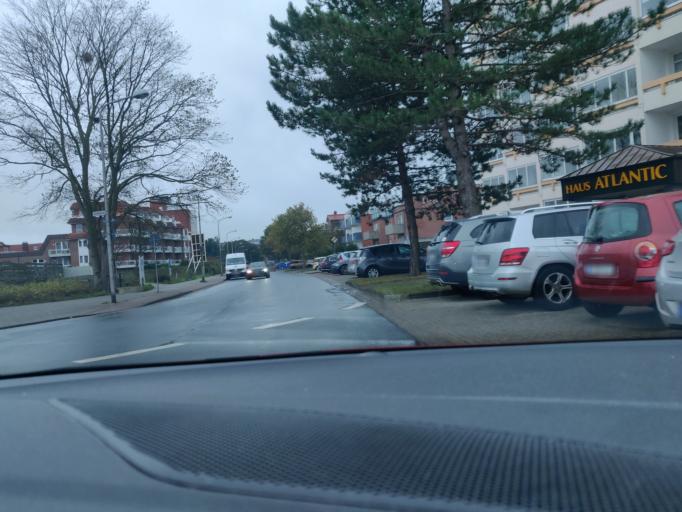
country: DE
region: Lower Saxony
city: Cuxhaven
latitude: 53.8891
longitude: 8.6663
